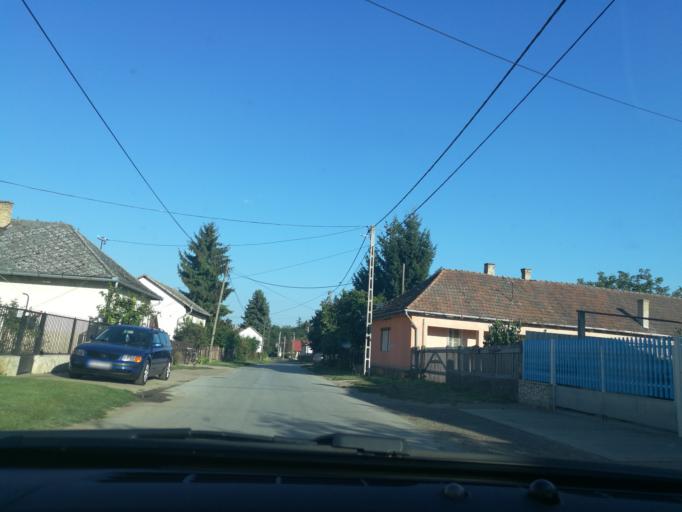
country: HU
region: Szabolcs-Szatmar-Bereg
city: Tiszabercel
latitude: 48.1652
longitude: 21.5900
